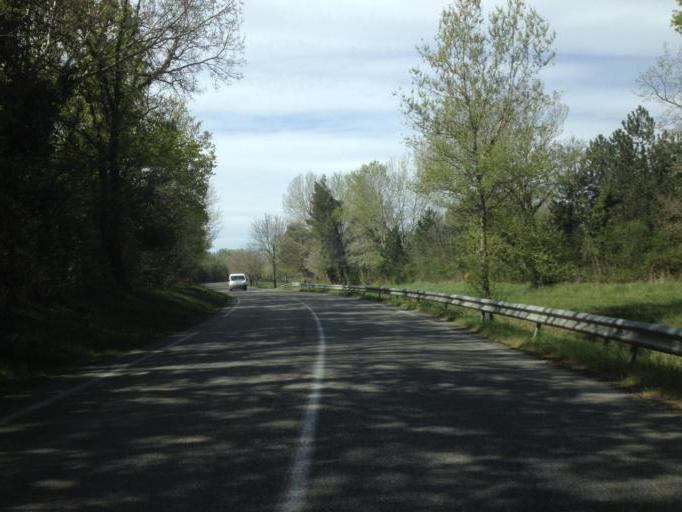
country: FR
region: Provence-Alpes-Cote d'Azur
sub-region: Departement du Vaucluse
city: Caderousse
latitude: 44.1333
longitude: 4.7332
